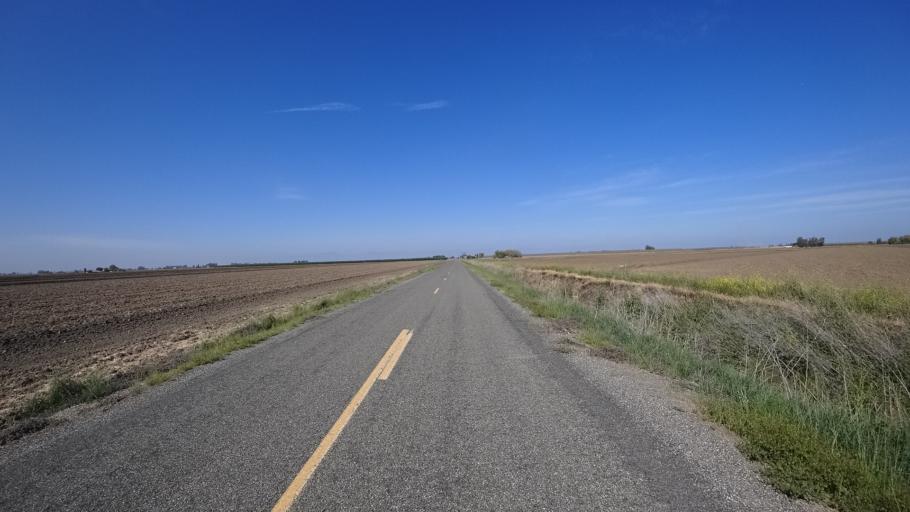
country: US
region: California
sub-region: Glenn County
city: Hamilton City
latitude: 39.6161
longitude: -122.0290
